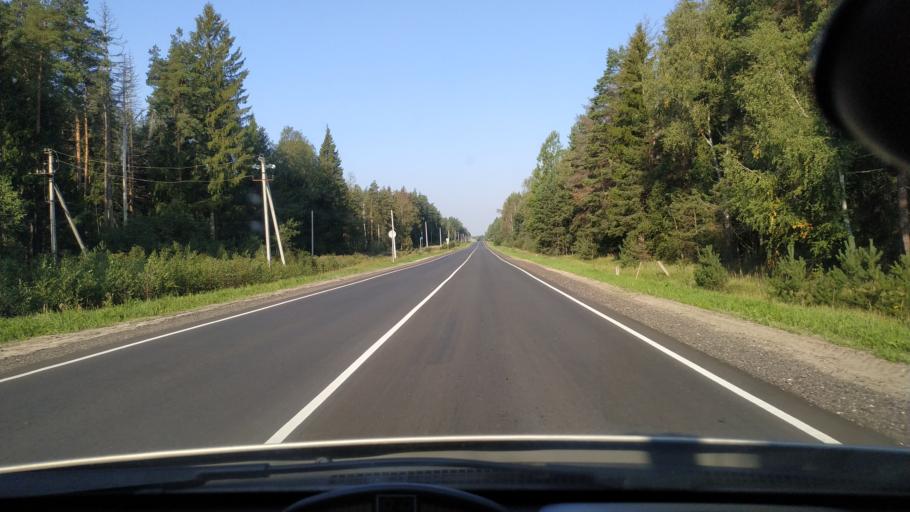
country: RU
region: Moskovskaya
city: Roshal'
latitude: 55.6574
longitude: 39.7950
